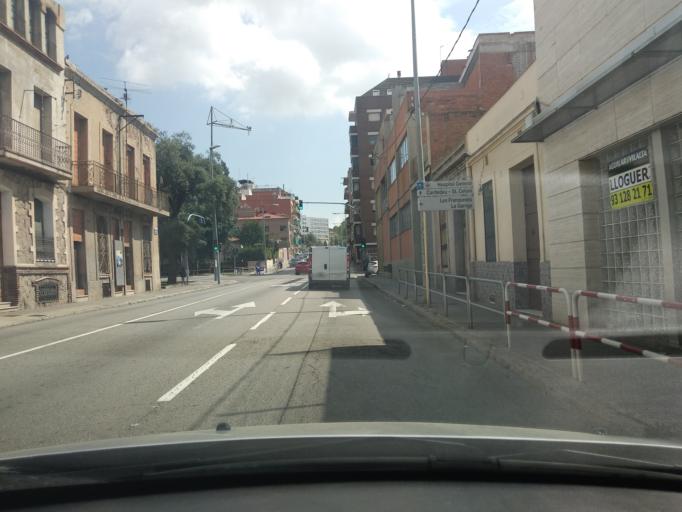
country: ES
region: Catalonia
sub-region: Provincia de Barcelona
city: Granollers
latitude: 41.6135
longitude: 2.2912
